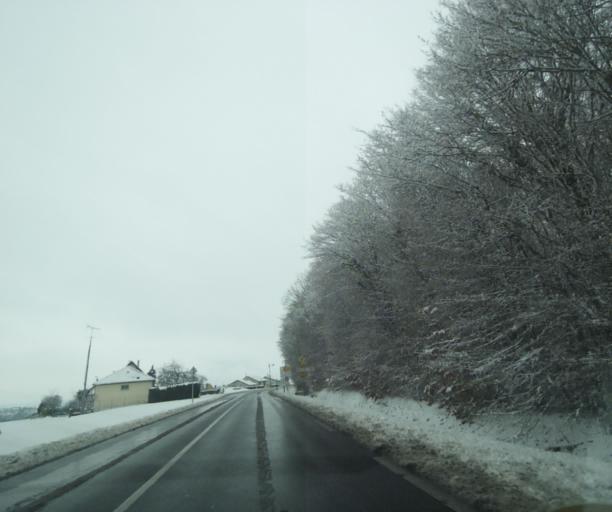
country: FR
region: Champagne-Ardenne
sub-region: Departement de la Haute-Marne
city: Montier-en-Der
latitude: 48.4857
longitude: 4.7746
